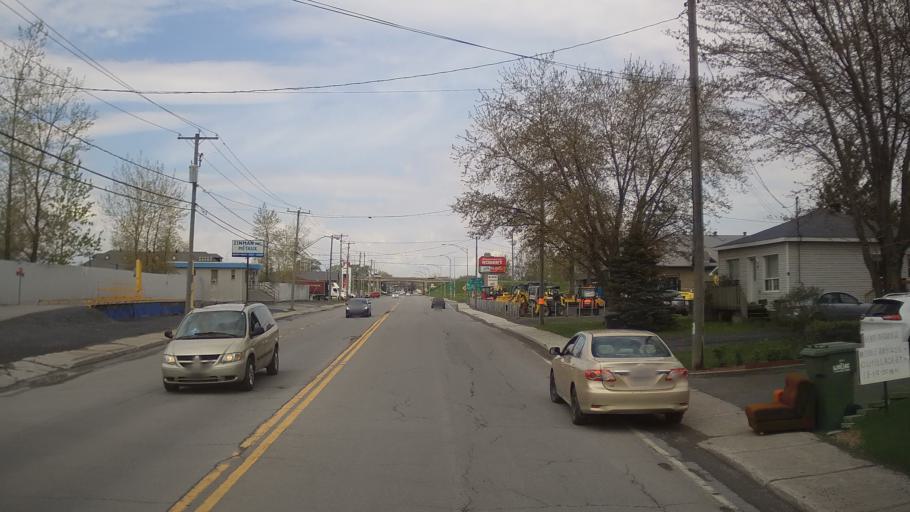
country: CA
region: Quebec
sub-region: Monteregie
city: Saint-Jean-sur-Richelieu
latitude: 45.3127
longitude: -73.2174
